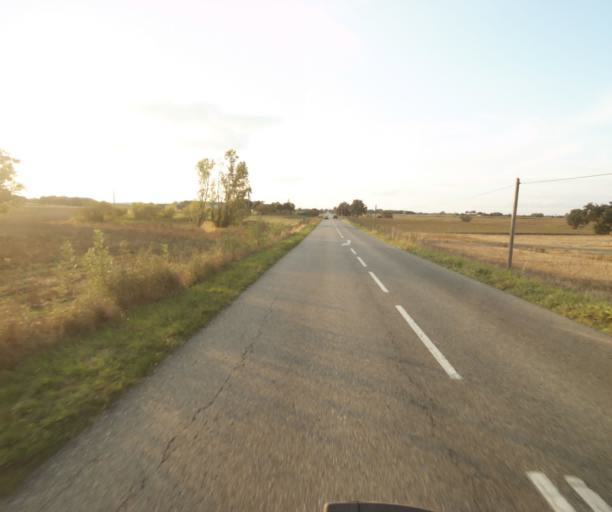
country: FR
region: Midi-Pyrenees
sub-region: Departement du Tarn-et-Garonne
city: Verdun-sur-Garonne
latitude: 43.8256
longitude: 1.1748
